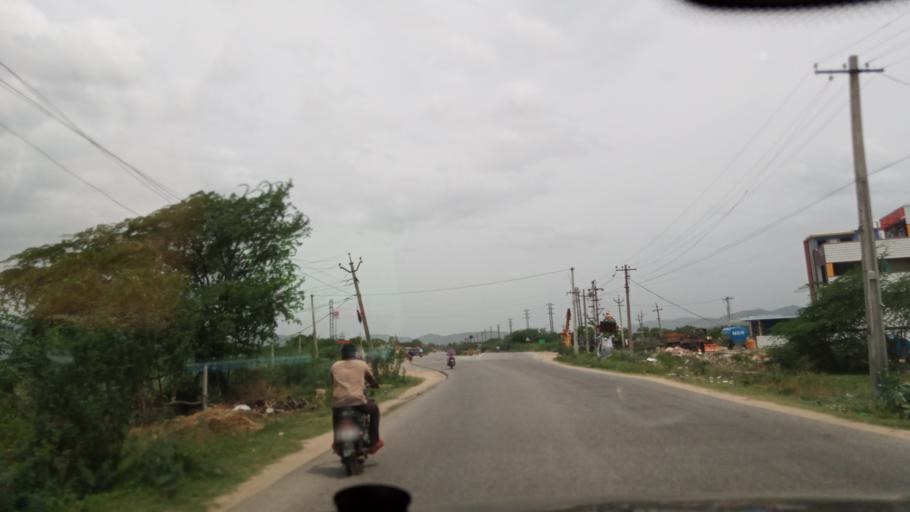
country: IN
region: Andhra Pradesh
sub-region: Chittoor
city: Renigunta
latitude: 13.5951
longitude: 79.5119
